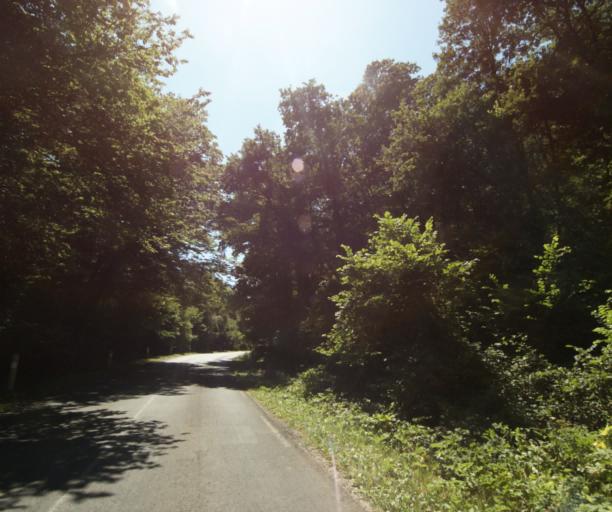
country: FR
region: Ile-de-France
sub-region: Departement de l'Essonne
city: Milly-la-Foret
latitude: 48.3607
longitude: 2.4645
